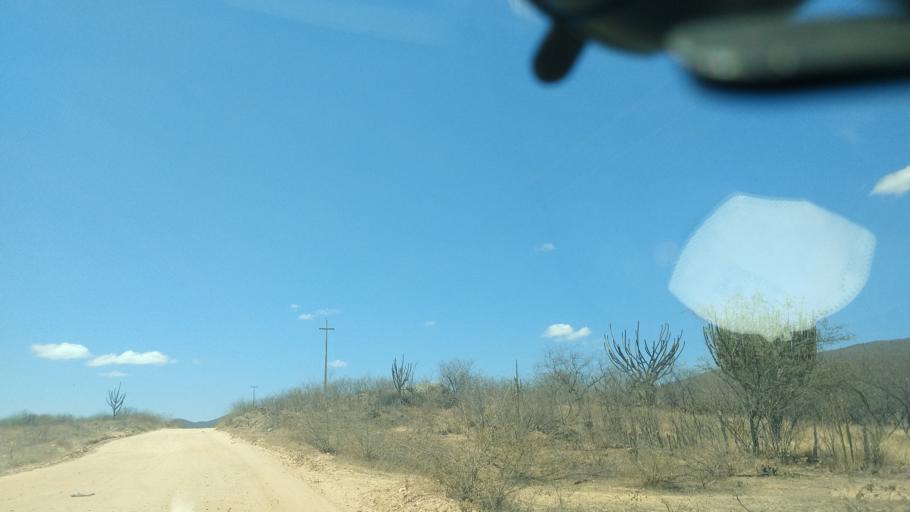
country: BR
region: Rio Grande do Norte
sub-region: Sao Tome
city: Sao Tome
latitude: -5.9774
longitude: -36.1714
